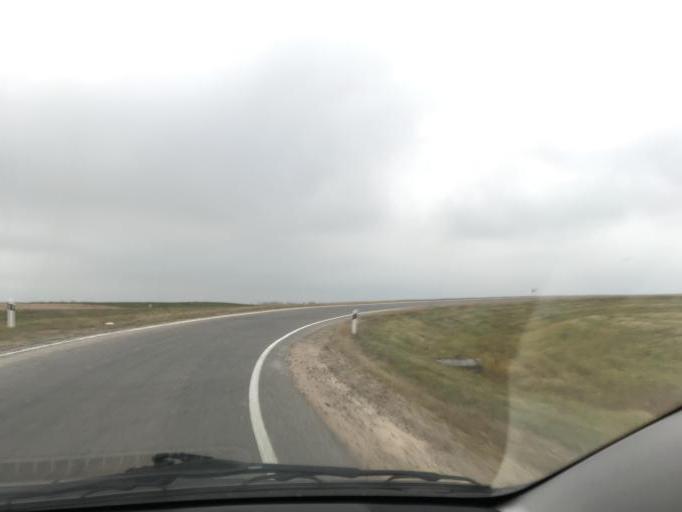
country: BY
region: Vitebsk
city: Vitebsk
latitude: 55.1555
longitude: 30.0639
